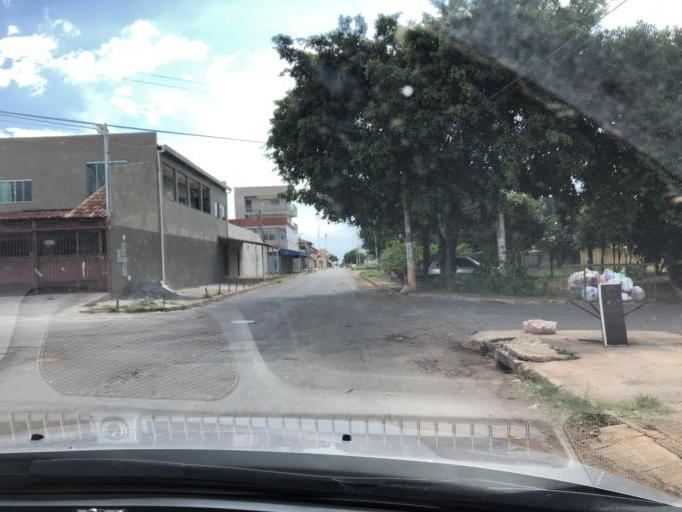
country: BR
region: Federal District
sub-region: Brasilia
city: Brasilia
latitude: -15.7904
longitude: -48.1194
